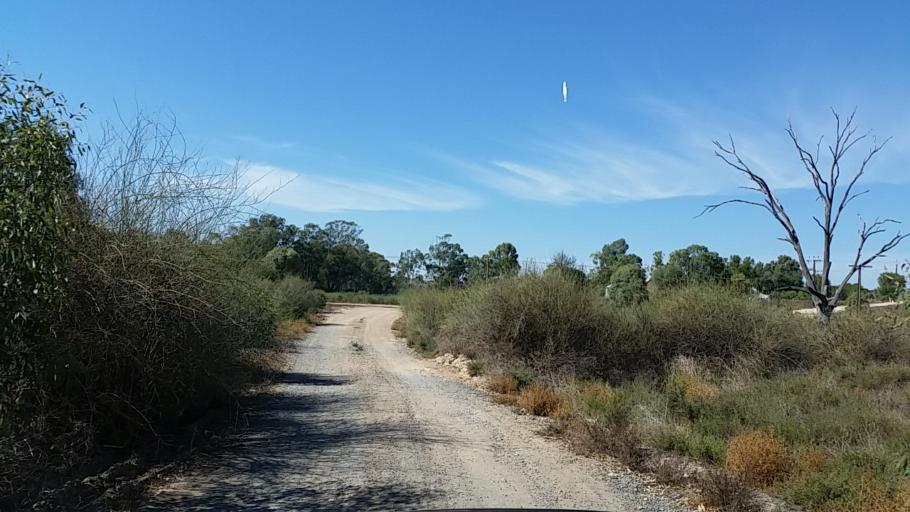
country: AU
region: South Australia
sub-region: Mid Murray
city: Mannum
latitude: -34.7508
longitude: 139.5559
